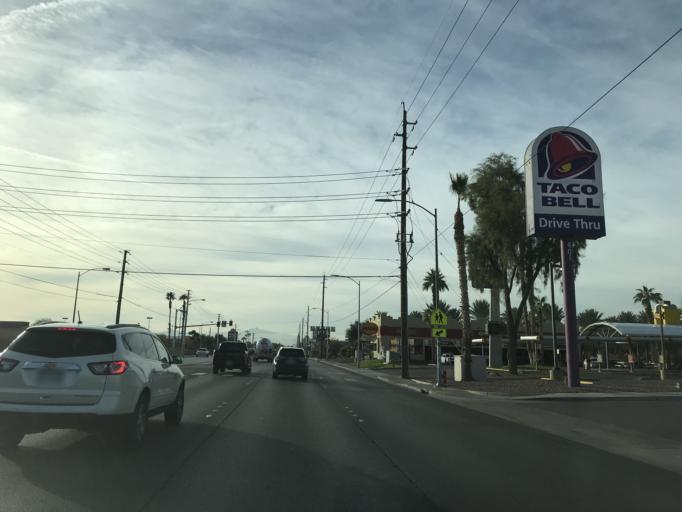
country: US
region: Nevada
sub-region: Clark County
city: Sunrise Manor
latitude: 36.1707
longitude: -115.0622
